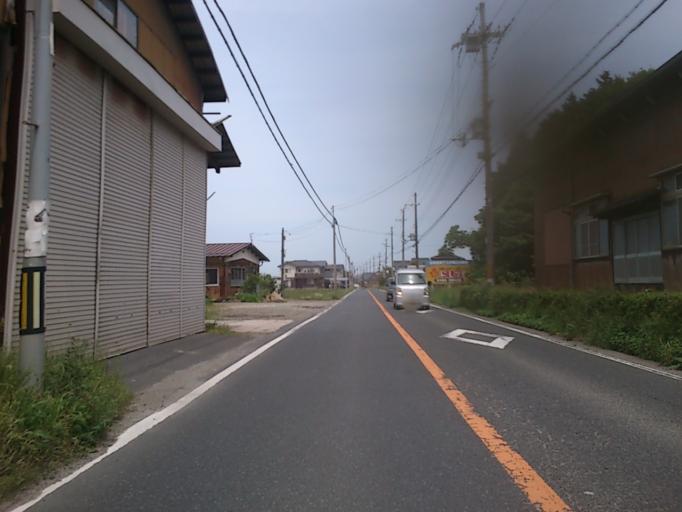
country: JP
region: Kyoto
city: Miyazu
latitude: 35.5946
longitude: 135.0972
